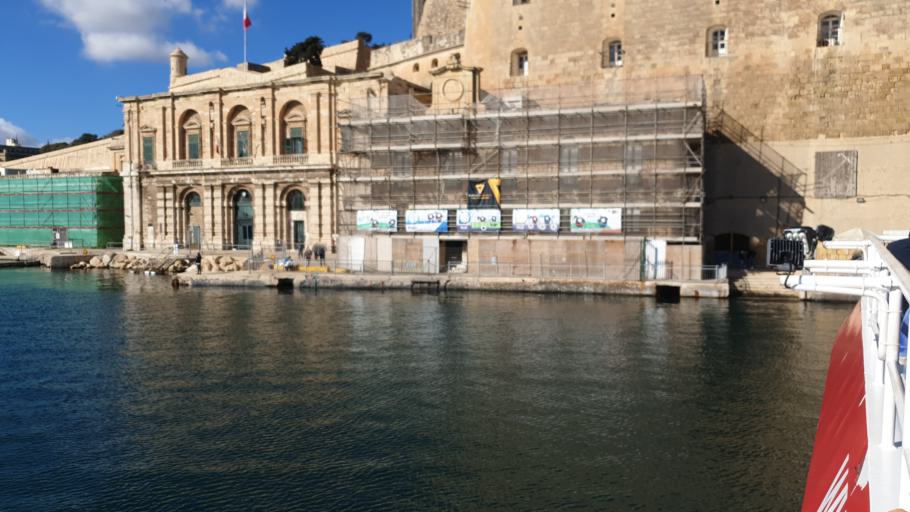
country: MT
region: Il-Birgu
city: Vittoriosa
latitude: 35.8940
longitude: 14.5137
